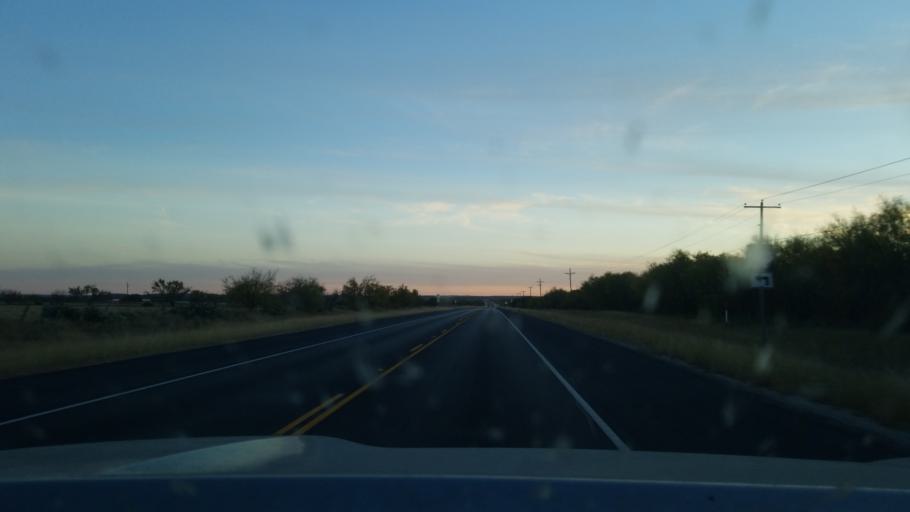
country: US
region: Texas
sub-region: Stephens County
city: Breckenridge
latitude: 32.6654
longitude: -98.9024
